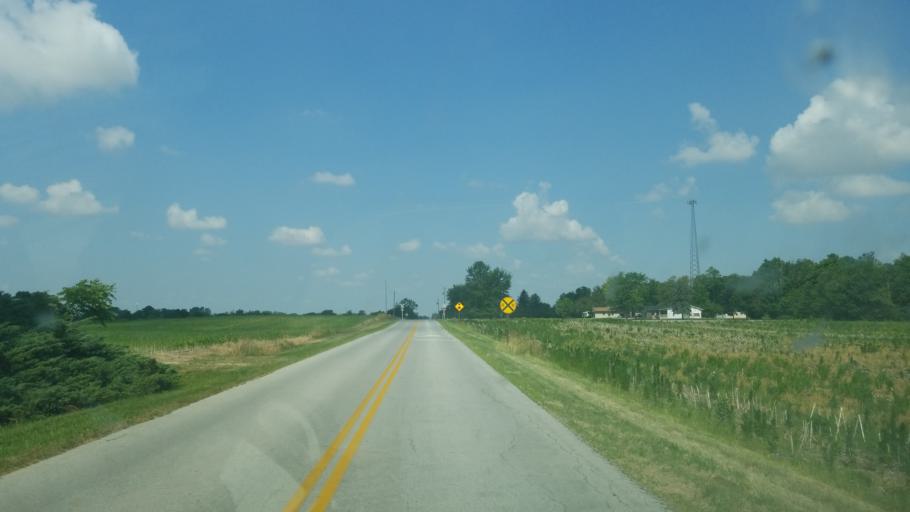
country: US
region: Ohio
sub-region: Auglaize County
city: Cridersville
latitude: 40.5711
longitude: -84.0767
